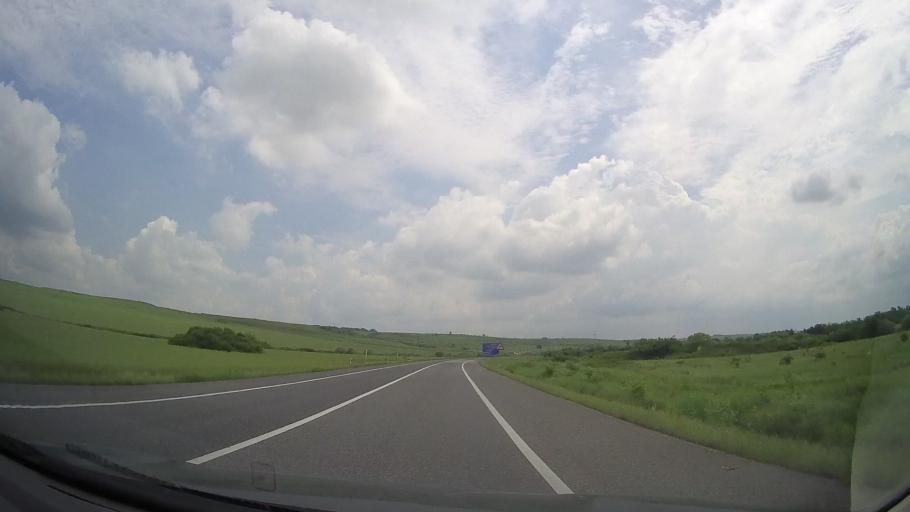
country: RO
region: Timis
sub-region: Municipiul Lugoj
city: Lugoj
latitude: 45.7218
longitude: 21.8891
